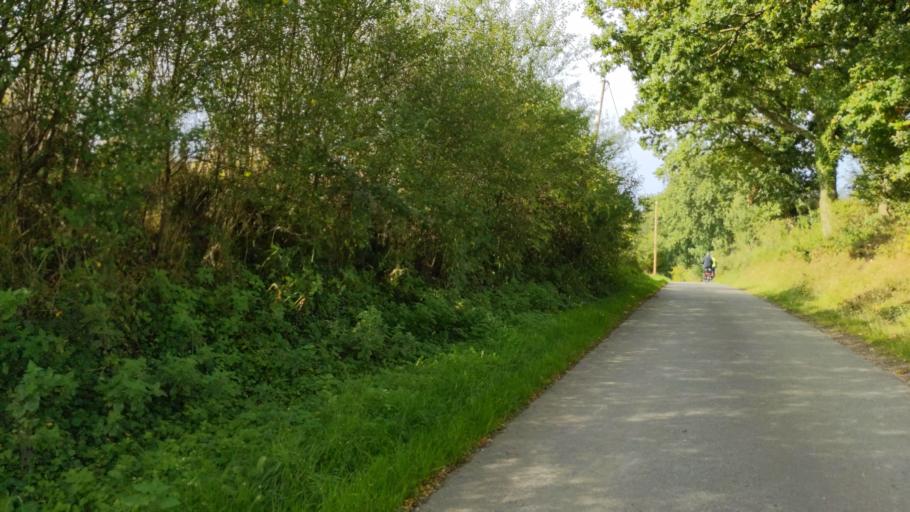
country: DE
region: Schleswig-Holstein
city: Zarpen
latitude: 53.8820
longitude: 10.5063
